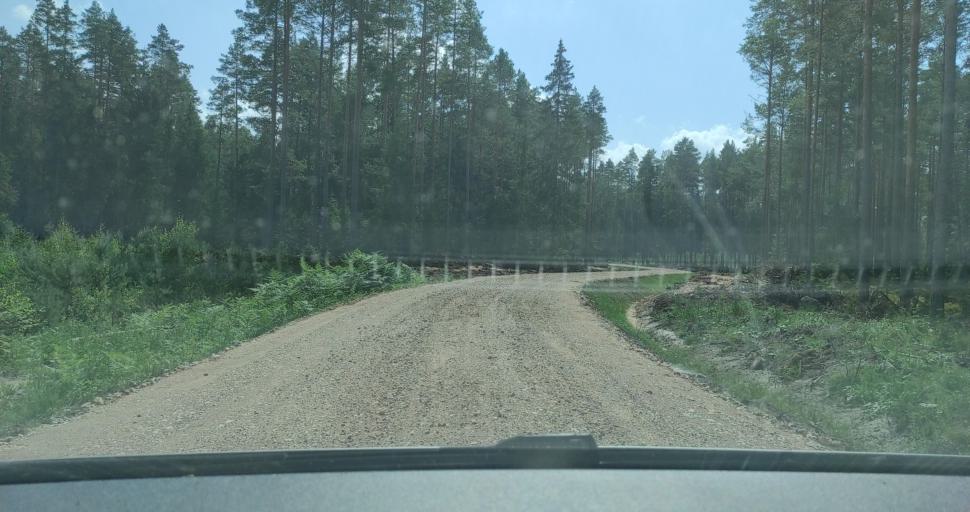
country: LV
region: Kuldigas Rajons
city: Kuldiga
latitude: 57.0672
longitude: 22.1936
